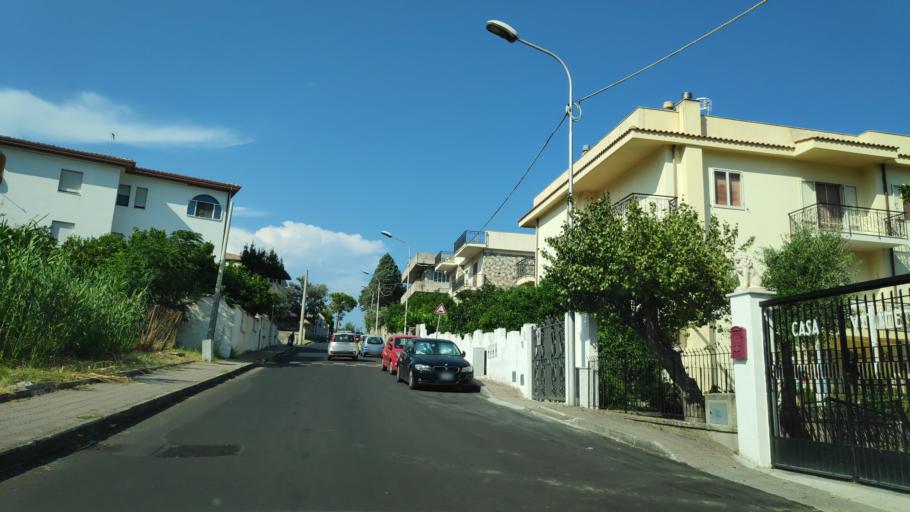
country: IT
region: Calabria
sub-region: Provincia di Catanzaro
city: Martelli-Laganosa
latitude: 38.6805
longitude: 16.5425
